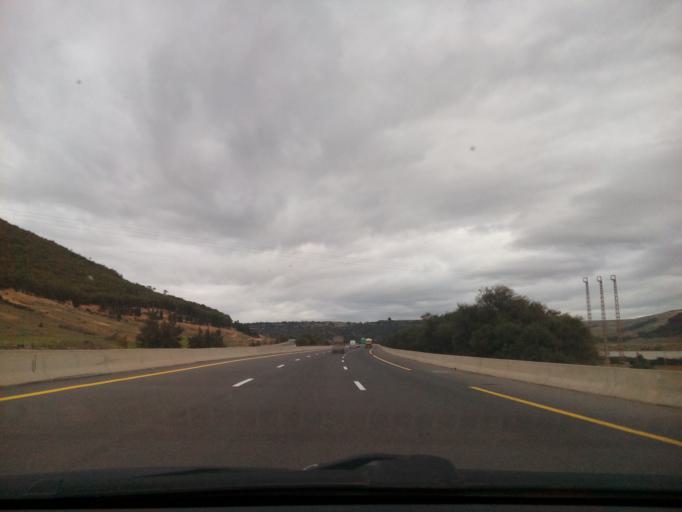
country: DZ
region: Sidi Bel Abbes
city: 'Ain el Berd
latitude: 35.3854
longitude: -0.4964
